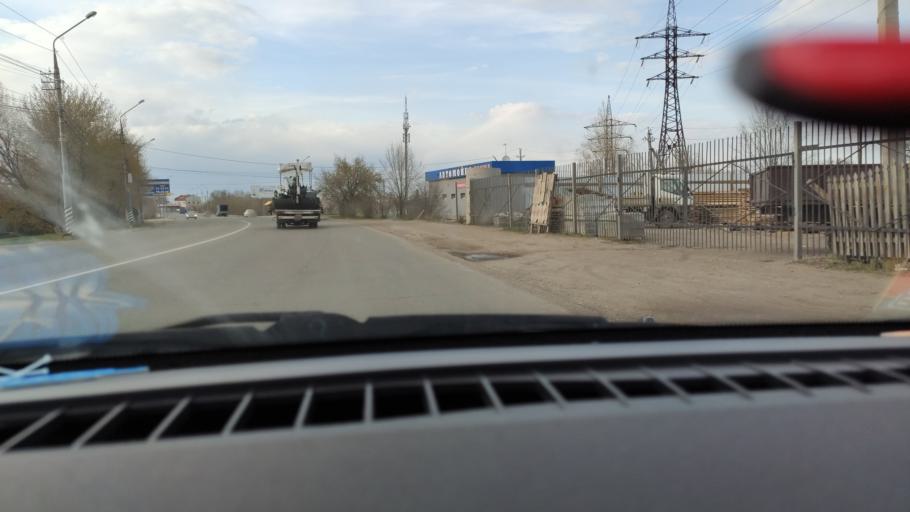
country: RU
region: Saratov
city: Privolzhskiy
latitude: 51.4239
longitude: 46.0465
